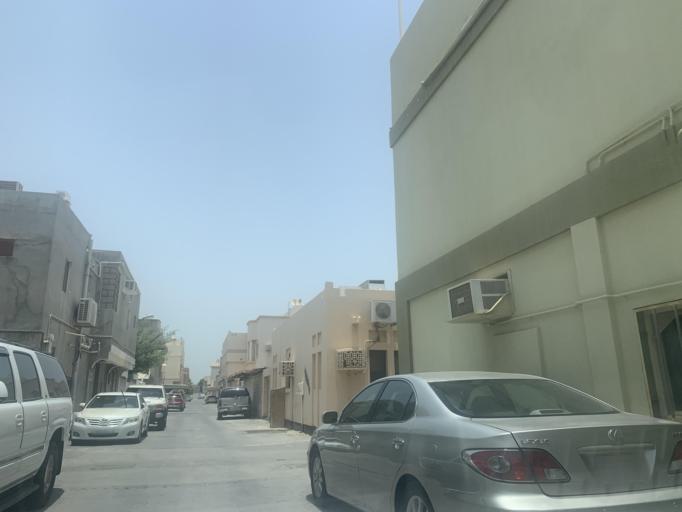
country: BH
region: Manama
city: Jidd Hafs
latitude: 26.2162
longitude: 50.4600
